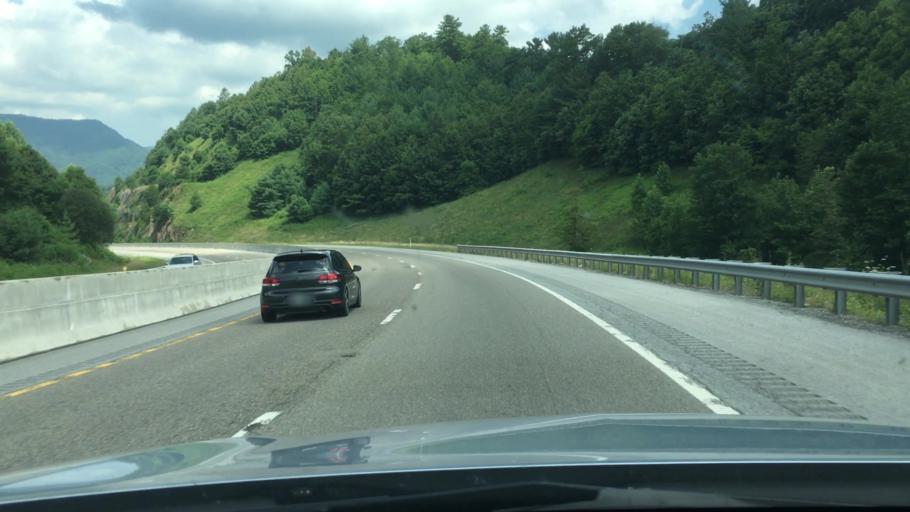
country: US
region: Tennessee
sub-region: Unicoi County
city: Banner Hill
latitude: 36.0028
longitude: -82.5394
